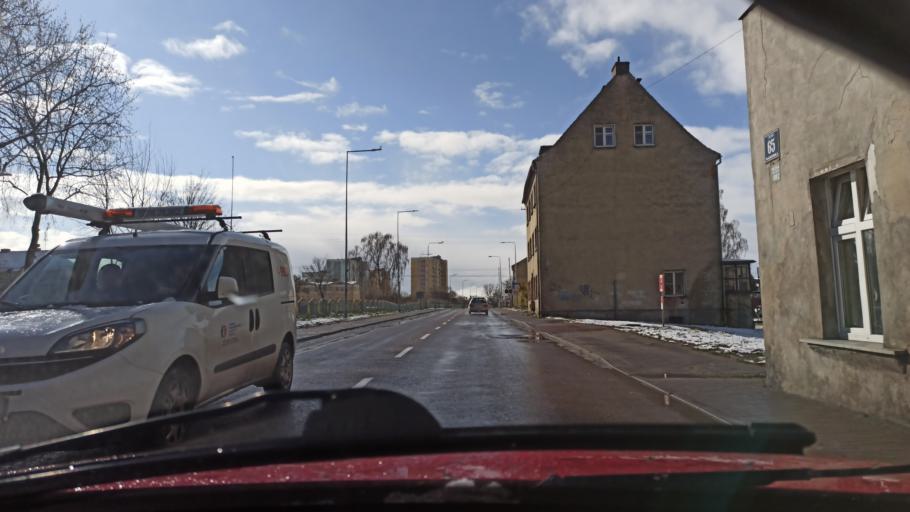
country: PL
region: Warmian-Masurian Voivodeship
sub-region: Powiat elblaski
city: Elblag
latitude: 54.1513
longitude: 19.4026
